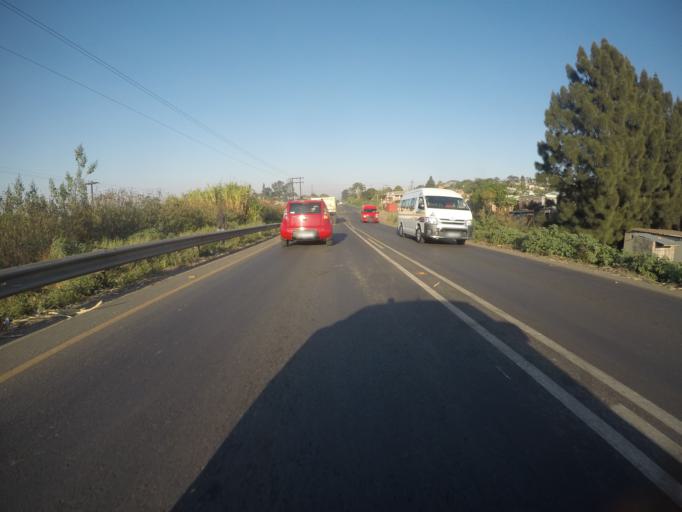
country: ZA
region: KwaZulu-Natal
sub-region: iLembe District Municipality
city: Stanger
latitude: -29.4112
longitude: 31.2452
